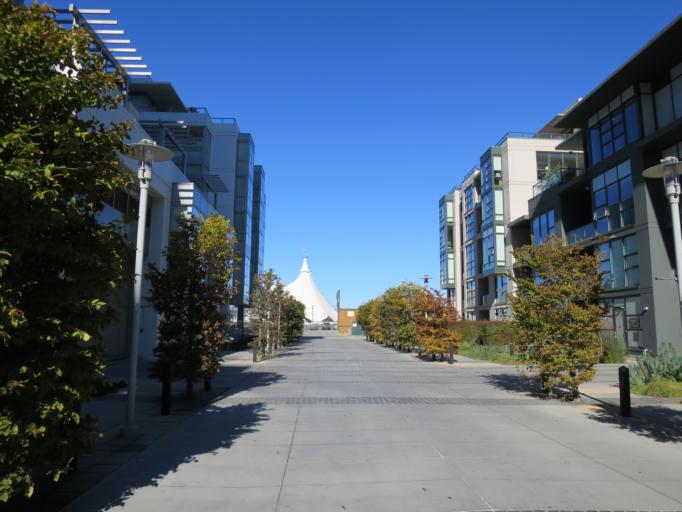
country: US
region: California
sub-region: San Francisco County
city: San Francisco
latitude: 37.7715
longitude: -122.3879
